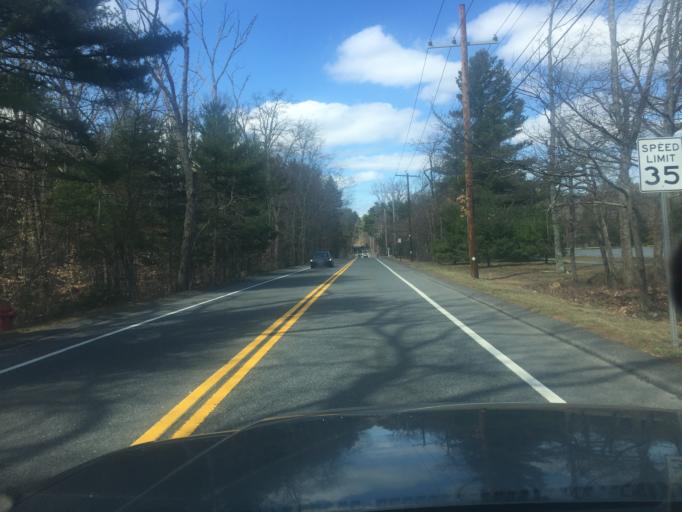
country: US
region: Massachusetts
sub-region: Norfolk County
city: Norfolk
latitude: 42.1030
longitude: -71.3087
